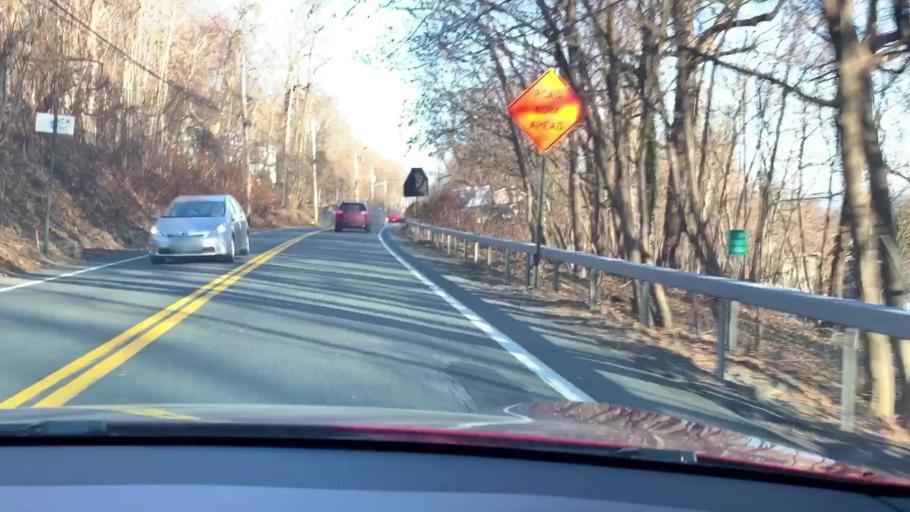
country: US
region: New York
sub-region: Rockland County
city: South Nyack
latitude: 41.0747
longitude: -73.9230
